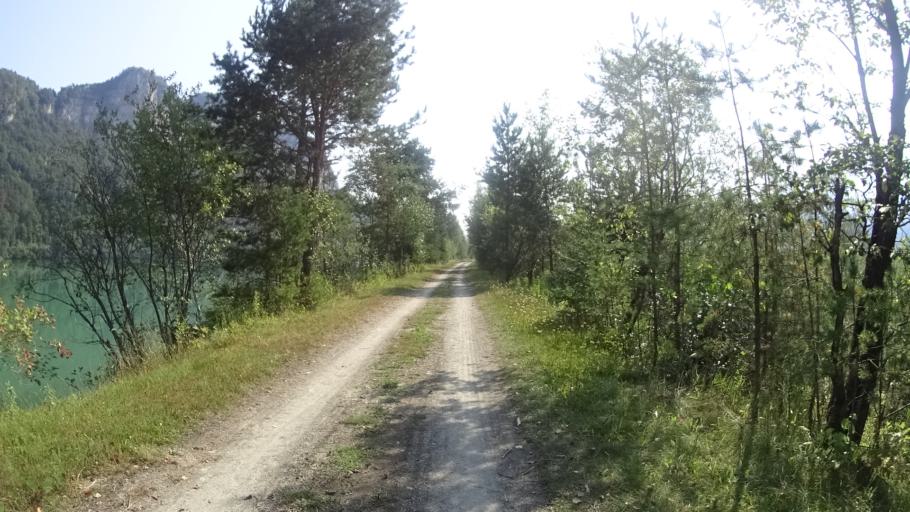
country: AT
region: Carinthia
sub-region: Politischer Bezirk Klagenfurt Land
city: Ebenthal
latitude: 46.5525
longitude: 14.3861
